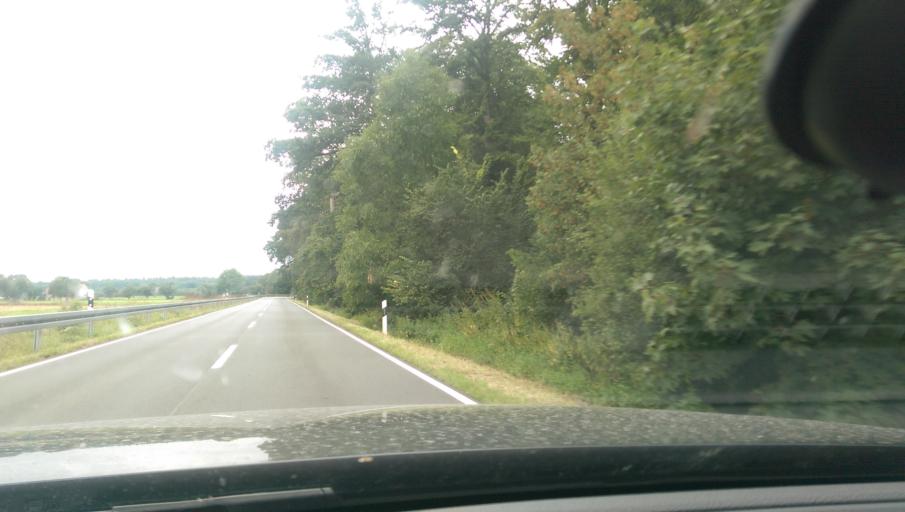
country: DE
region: Lower Saxony
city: Neustadt am Rubenberge
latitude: 52.5558
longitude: 9.4965
